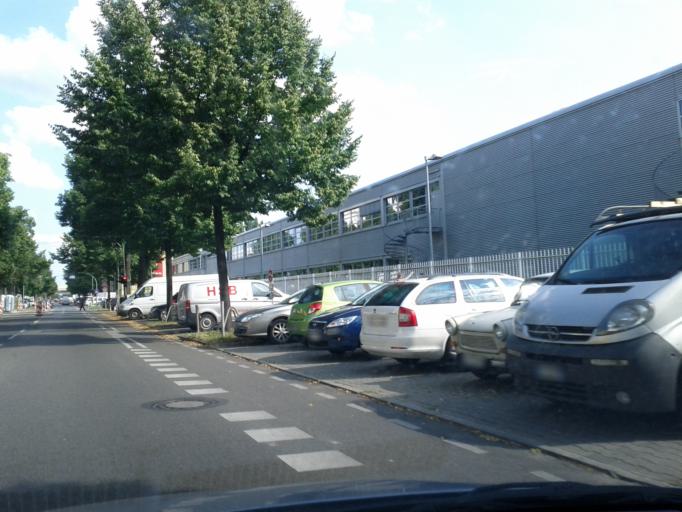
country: DE
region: Berlin
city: Treptow Bezirk
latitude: 52.4880
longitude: 13.4554
